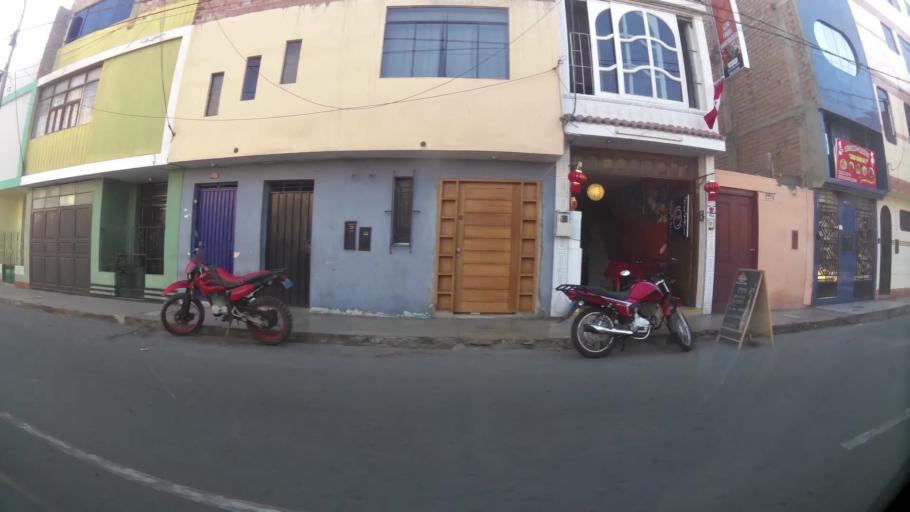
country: PE
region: Lima
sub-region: Huaura
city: Huacho
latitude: -11.1079
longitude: -77.6118
